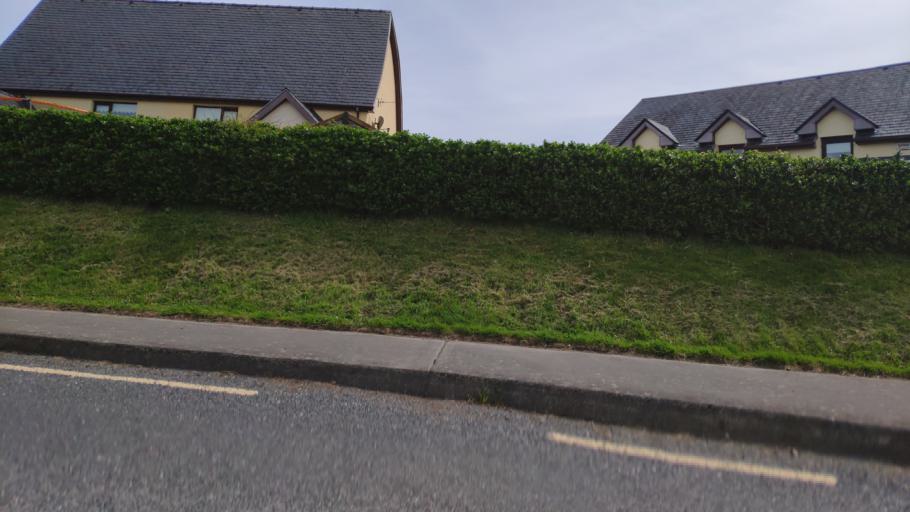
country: IE
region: Munster
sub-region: County Cork
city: Blarney
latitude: 51.9795
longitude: -8.5137
